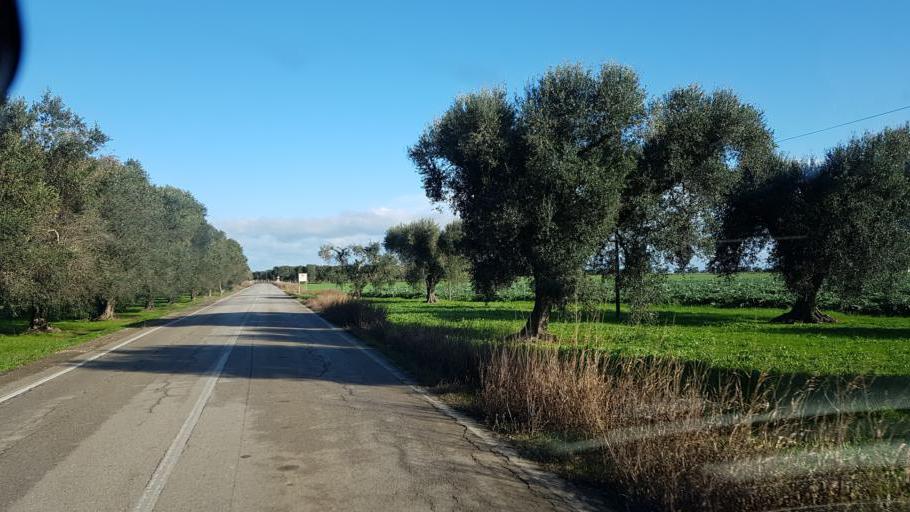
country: IT
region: Apulia
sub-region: Provincia di Brindisi
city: Tuturano
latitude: 40.5602
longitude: 17.9480
